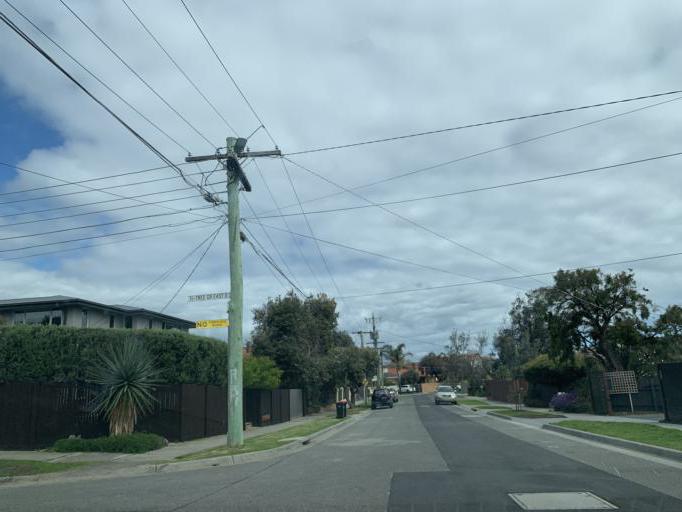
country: AU
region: Victoria
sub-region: Kingston
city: Parkdale
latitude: -37.9959
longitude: 145.0738
